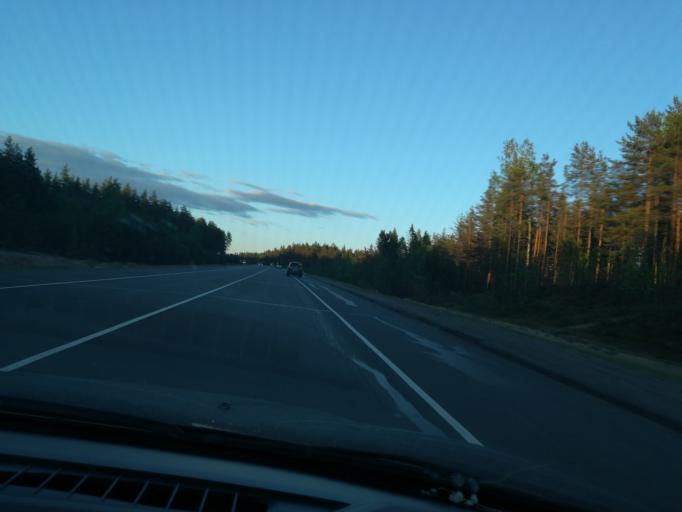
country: RU
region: Leningrad
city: Yakovlevo
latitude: 60.3616
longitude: 29.5681
